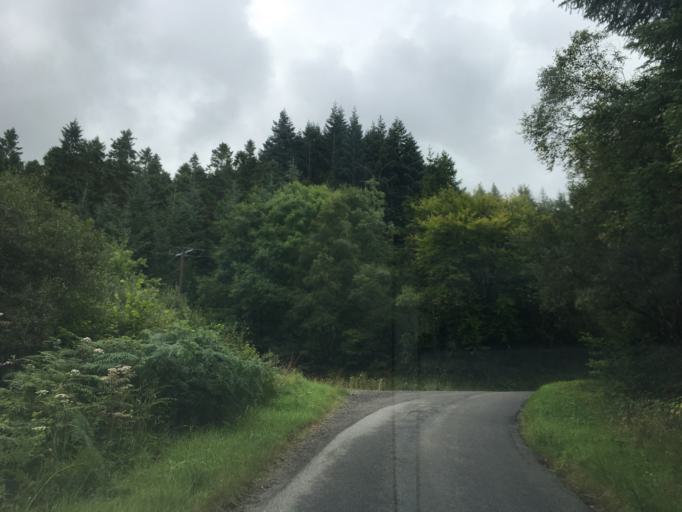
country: GB
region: Scotland
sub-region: Argyll and Bute
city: Oban
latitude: 56.2865
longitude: -5.3032
